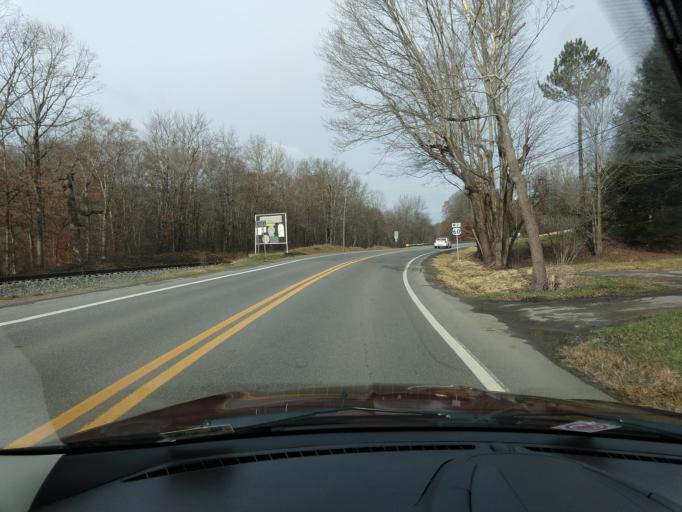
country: US
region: West Virginia
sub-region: Greenbrier County
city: Rainelle
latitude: 37.9647
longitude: -80.6979
